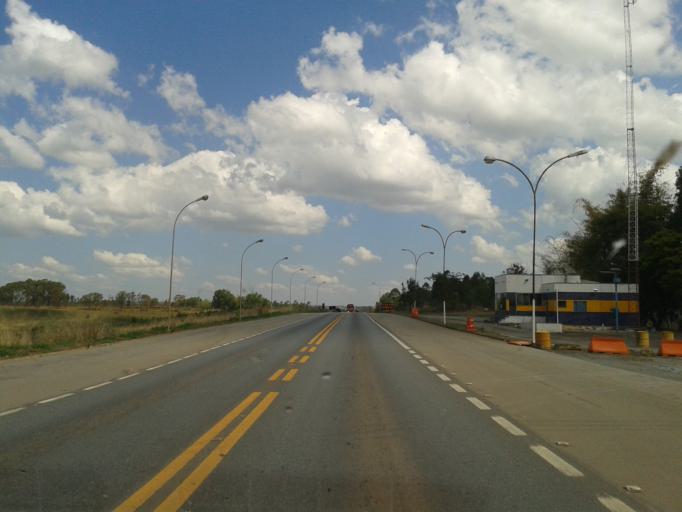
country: BR
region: Minas Gerais
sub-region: Campos Altos
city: Campos Altos
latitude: -19.6758
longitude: -46.0435
